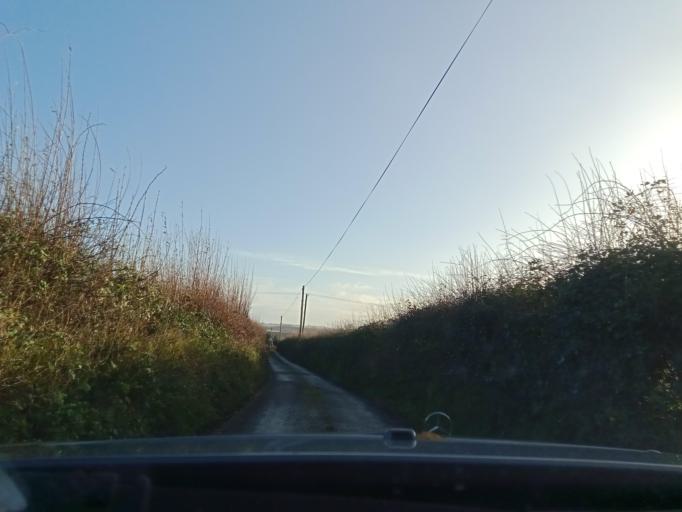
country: IE
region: Leinster
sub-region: Kilkenny
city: Callan
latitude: 52.4802
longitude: -7.3929
